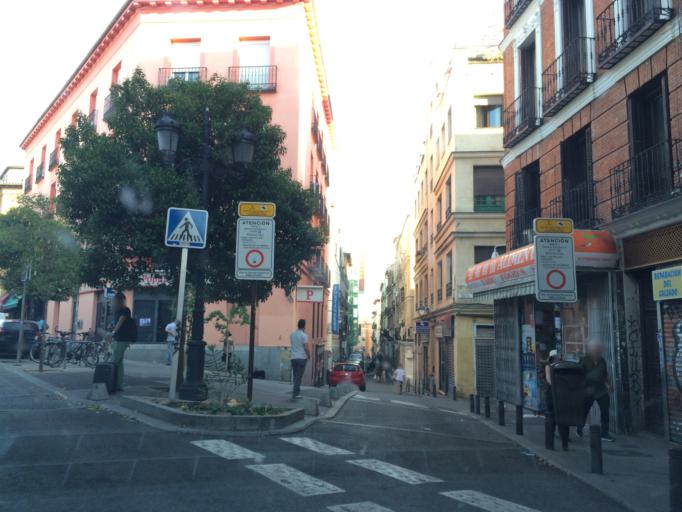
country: ES
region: Madrid
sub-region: Provincia de Madrid
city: Madrid
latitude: 40.4120
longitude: -3.6995
